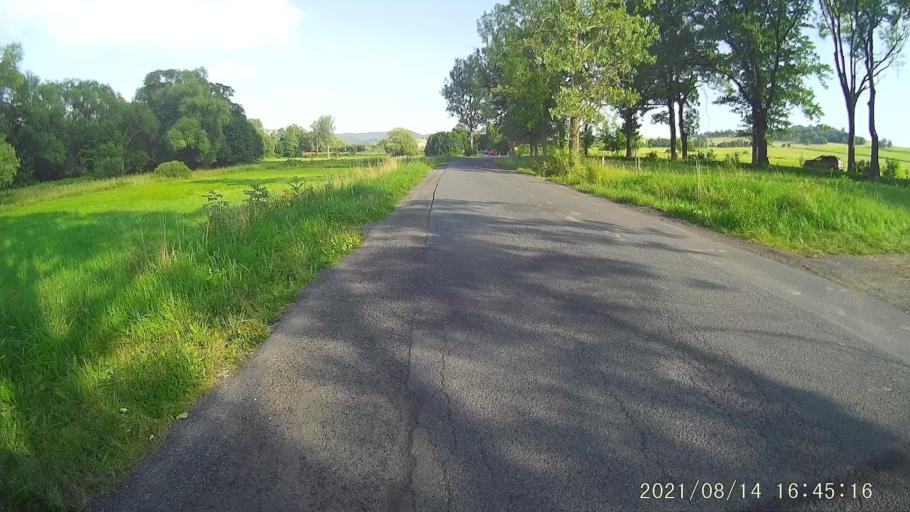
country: PL
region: Lower Silesian Voivodeship
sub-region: Powiat kamiennogorski
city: Kamienna Gora
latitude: 50.7763
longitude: 15.9690
